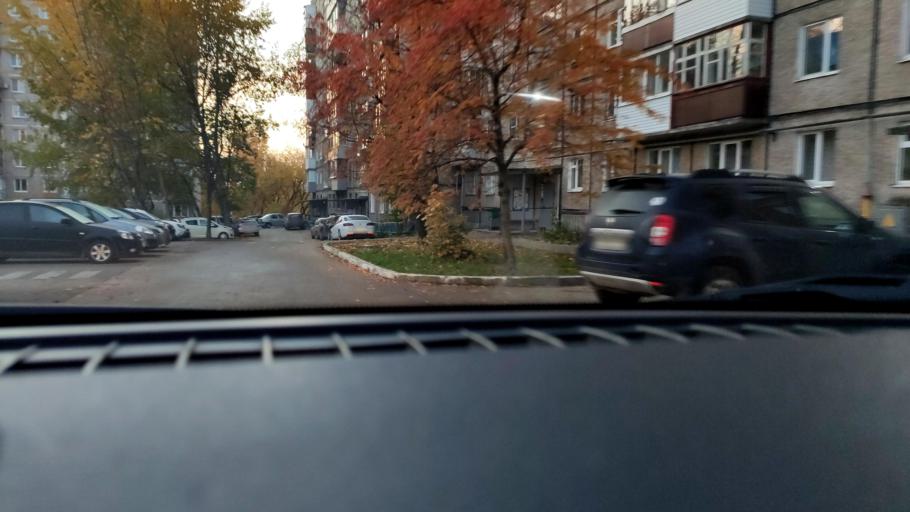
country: RU
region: Perm
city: Perm
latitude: 58.0221
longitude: 56.3008
